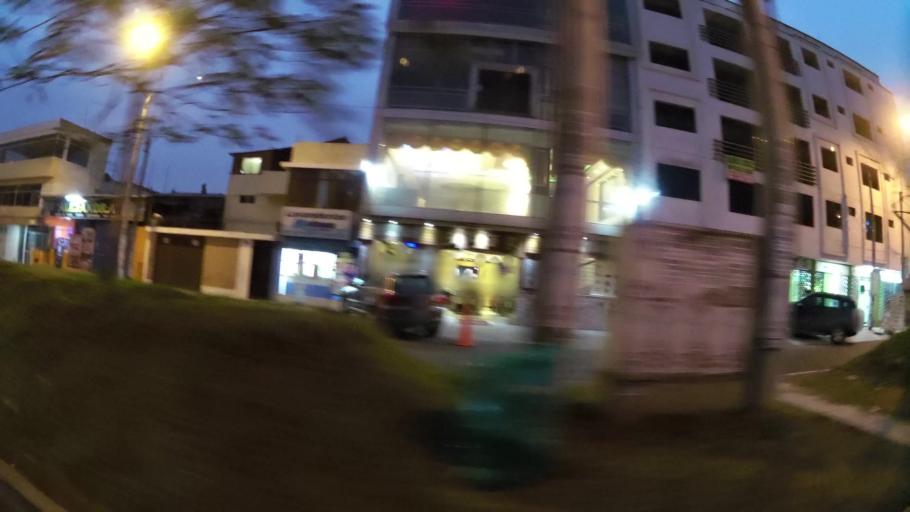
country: PE
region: Lima
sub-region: Lima
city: Surco
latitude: -12.1653
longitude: -76.9694
